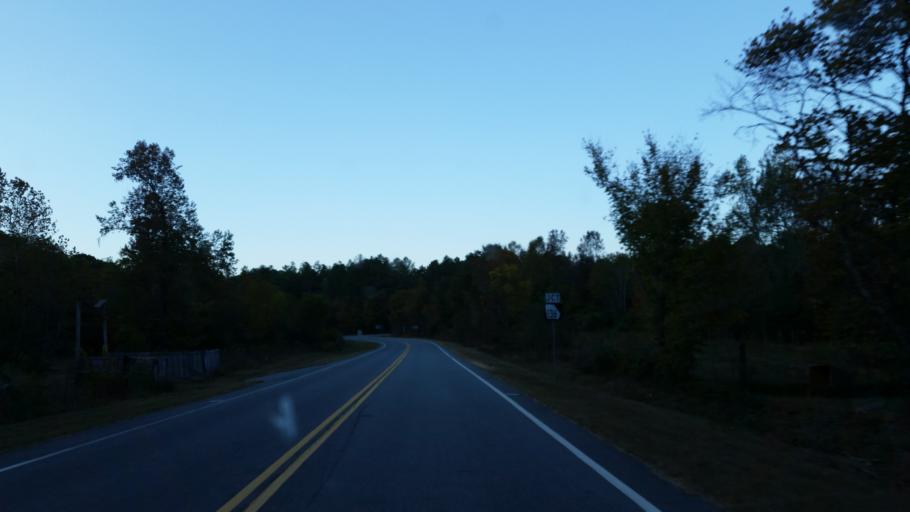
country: US
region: Georgia
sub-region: Gordon County
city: Calhoun
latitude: 34.6060
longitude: -85.0446
